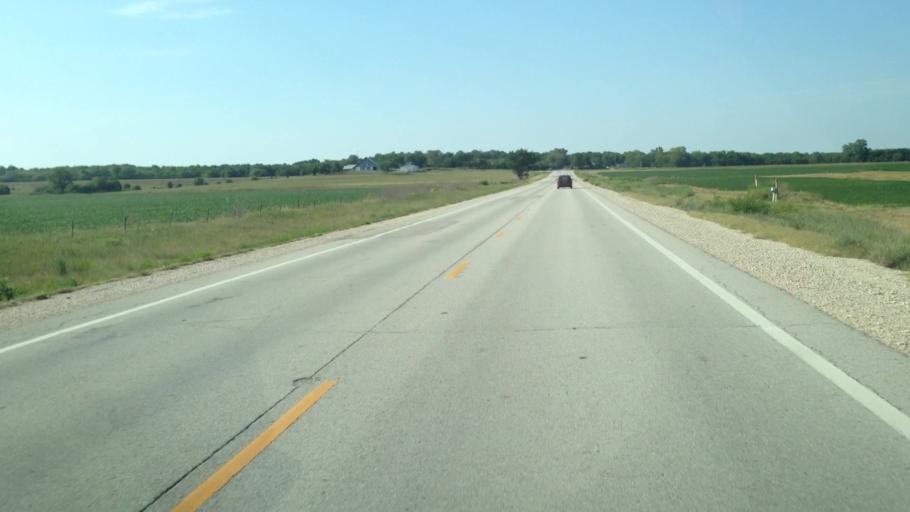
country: US
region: Kansas
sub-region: Anderson County
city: Garnett
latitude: 38.0741
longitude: -95.1694
